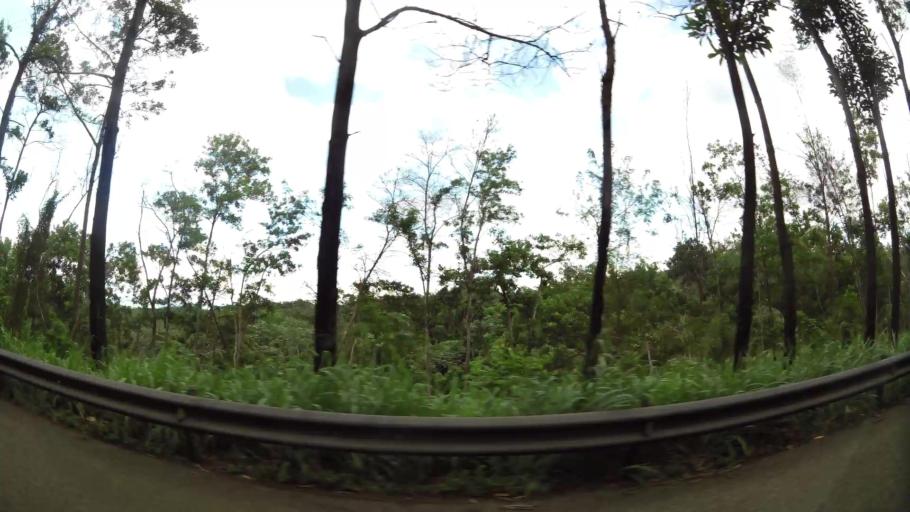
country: DO
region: La Vega
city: Rincon
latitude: 19.1159
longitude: -70.4468
